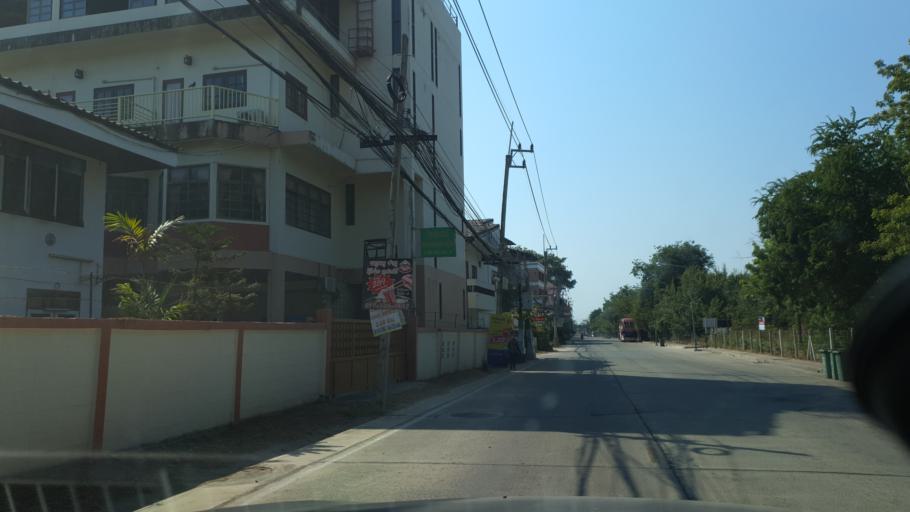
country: TH
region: Phetchaburi
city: Cha-am
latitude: 12.7983
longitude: 99.9832
